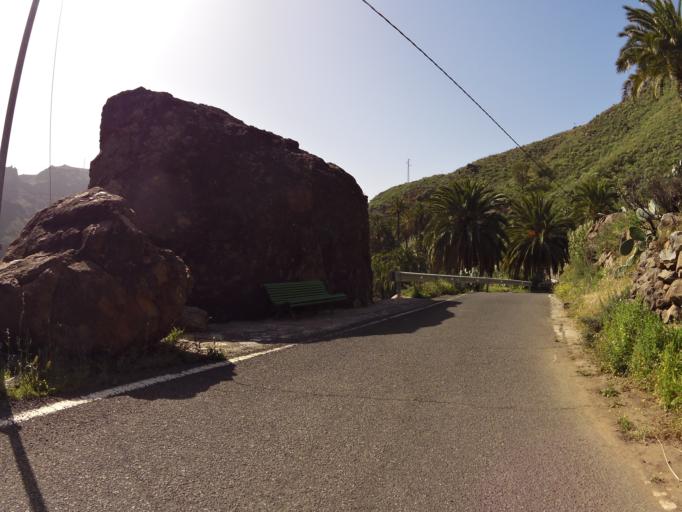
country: ES
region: Canary Islands
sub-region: Provincia de Las Palmas
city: Mogan
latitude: 27.9105
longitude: -15.6683
